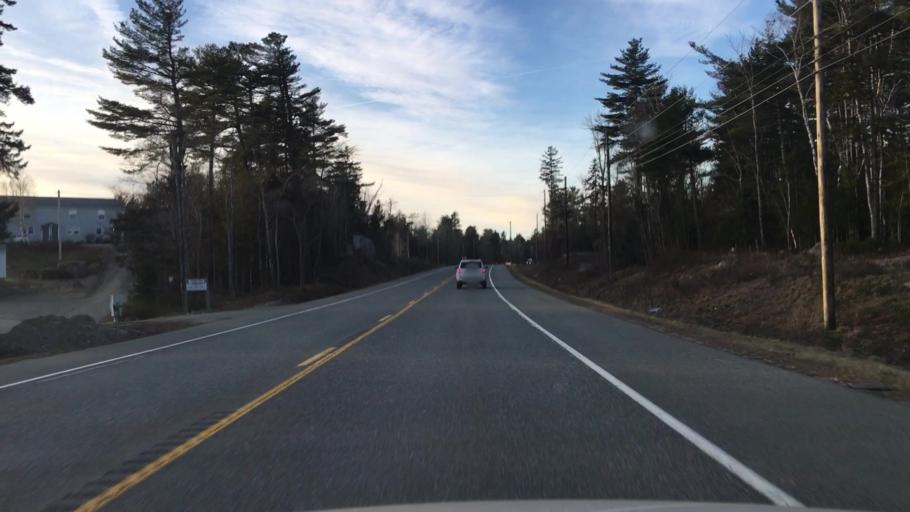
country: US
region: Maine
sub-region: Hancock County
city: Ellsworth
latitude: 44.5830
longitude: -68.4872
